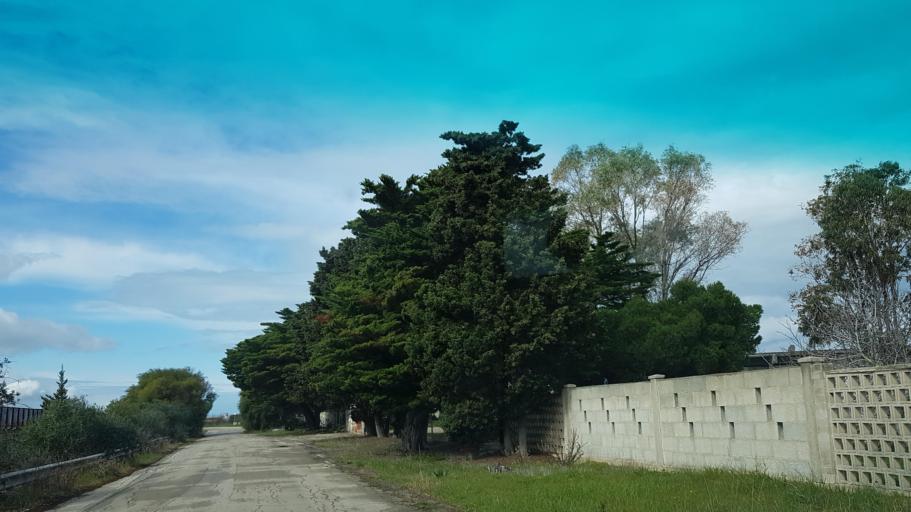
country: IT
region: Apulia
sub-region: Provincia di Brindisi
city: Materdomini
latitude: 40.6455
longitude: 17.9939
